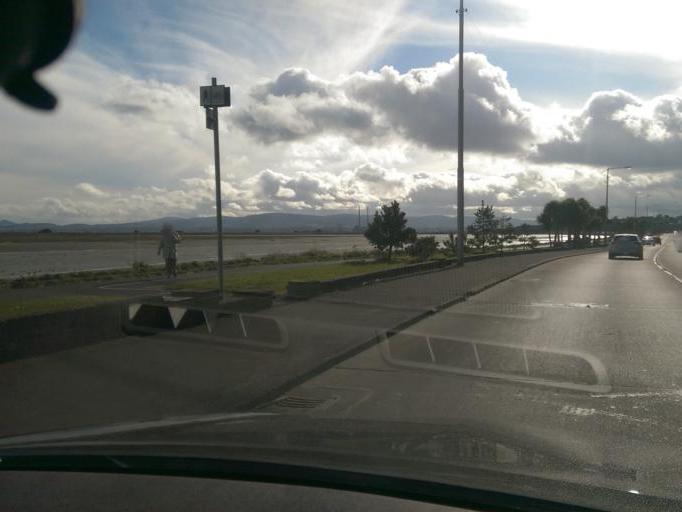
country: IE
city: Bayside
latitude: 53.3817
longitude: -6.1509
